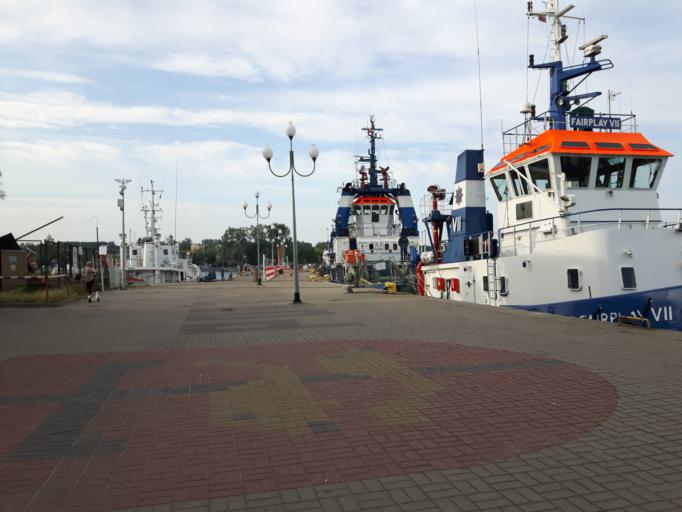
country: PL
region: Pomeranian Voivodeship
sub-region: Gdynia
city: Gdynia
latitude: 54.5337
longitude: 18.5478
